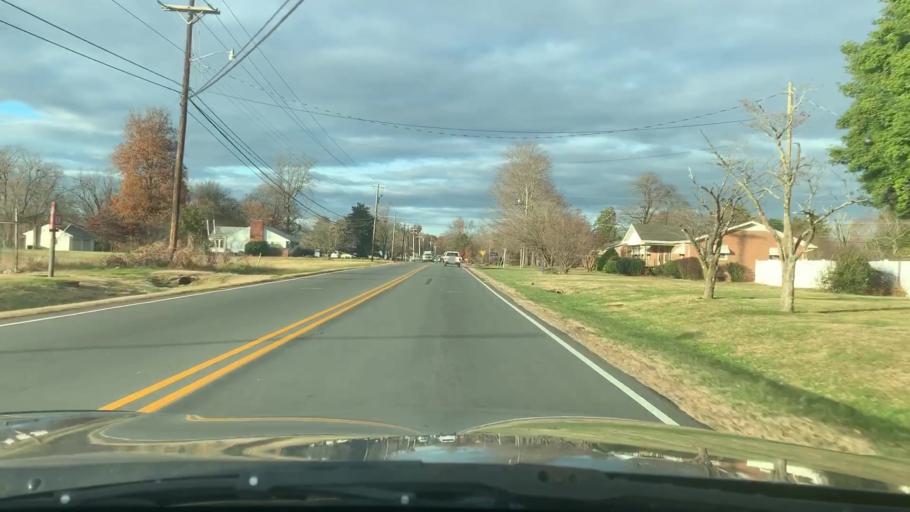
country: US
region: North Carolina
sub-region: Alamance County
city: Haw River
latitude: 36.0845
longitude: -79.3480
